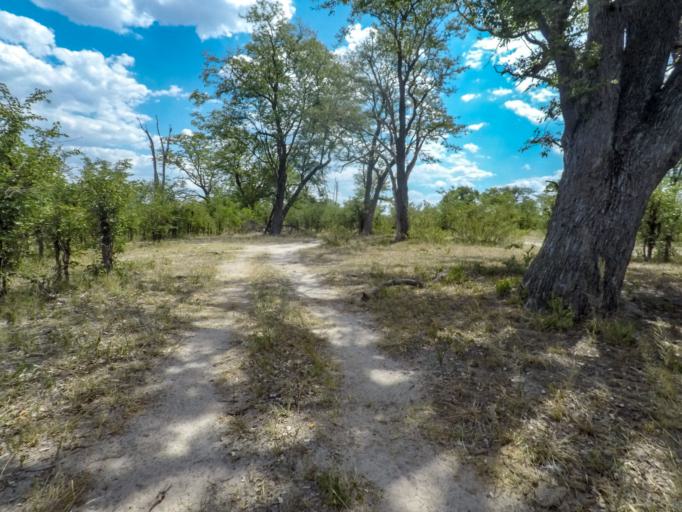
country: BW
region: North West
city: Maun
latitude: -19.2146
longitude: 23.6190
